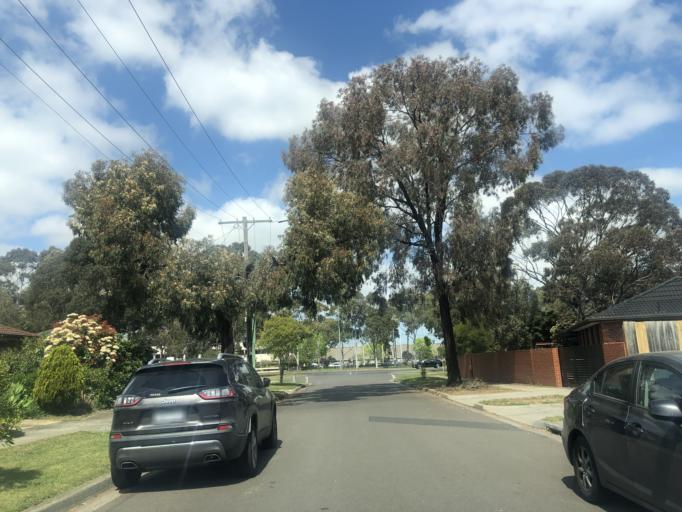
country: AU
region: Victoria
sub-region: Monash
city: Mulgrave
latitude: -37.9192
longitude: 145.1826
